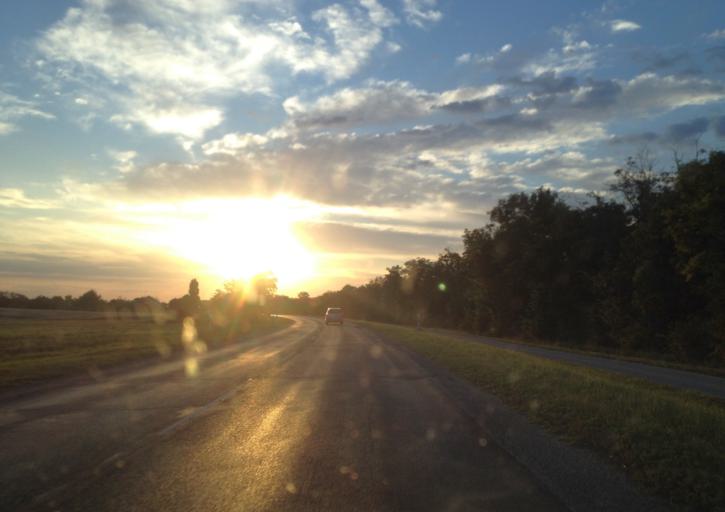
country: HU
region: Gyor-Moson-Sopron
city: Mosonmagyarovar
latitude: 47.8940
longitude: 17.2213
